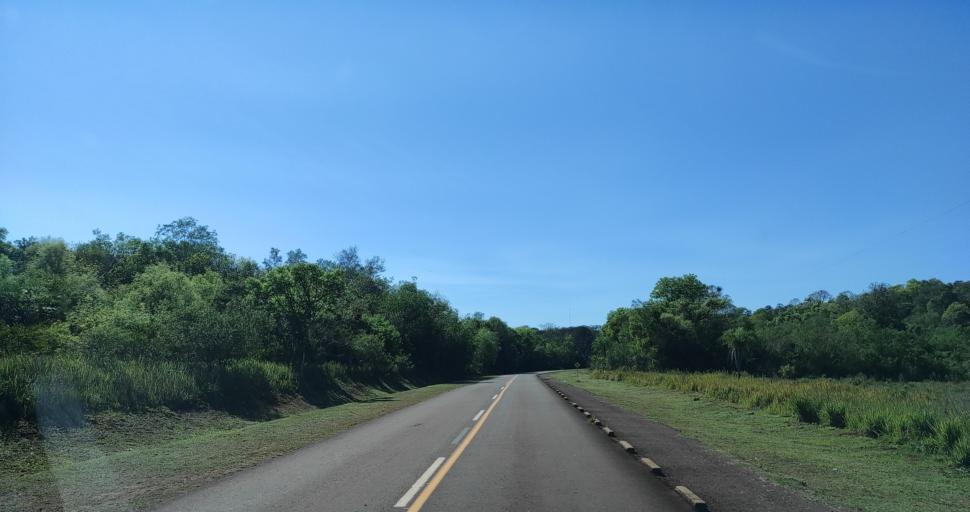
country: AR
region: Misiones
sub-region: Departamento de Candelaria
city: Loreto
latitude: -27.3371
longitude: -55.5360
